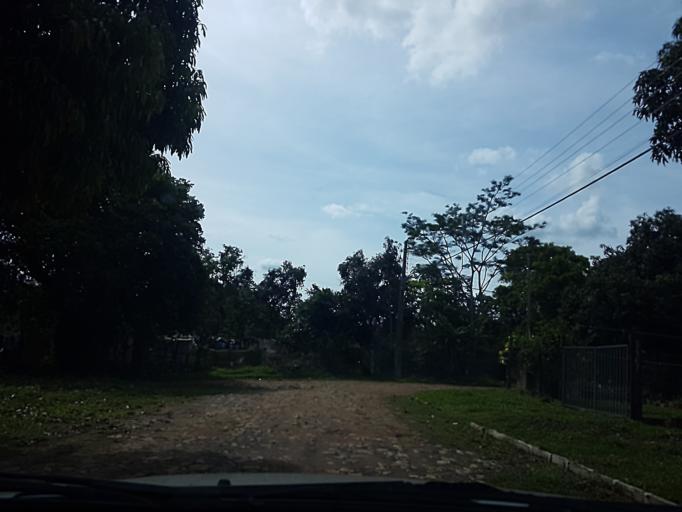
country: PY
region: Central
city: Colonia Mariano Roque Alonso
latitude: -25.1886
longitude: -57.5212
